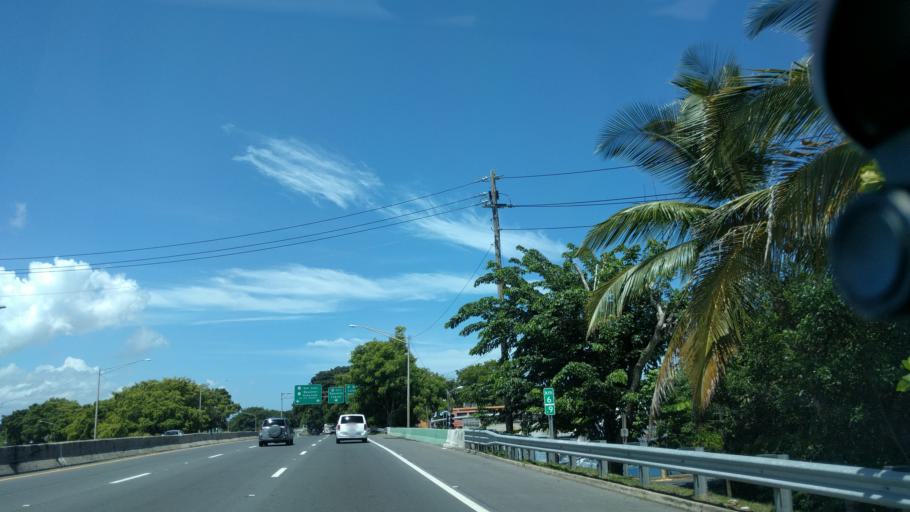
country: PR
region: San Juan
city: San Juan
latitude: 18.4401
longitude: -66.0654
